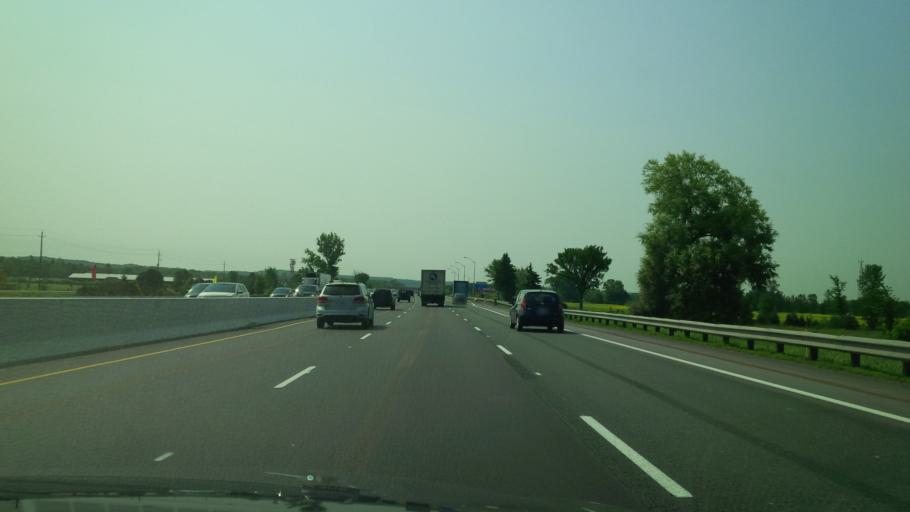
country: CA
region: Ontario
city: Innisfil
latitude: 44.2070
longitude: -79.6585
